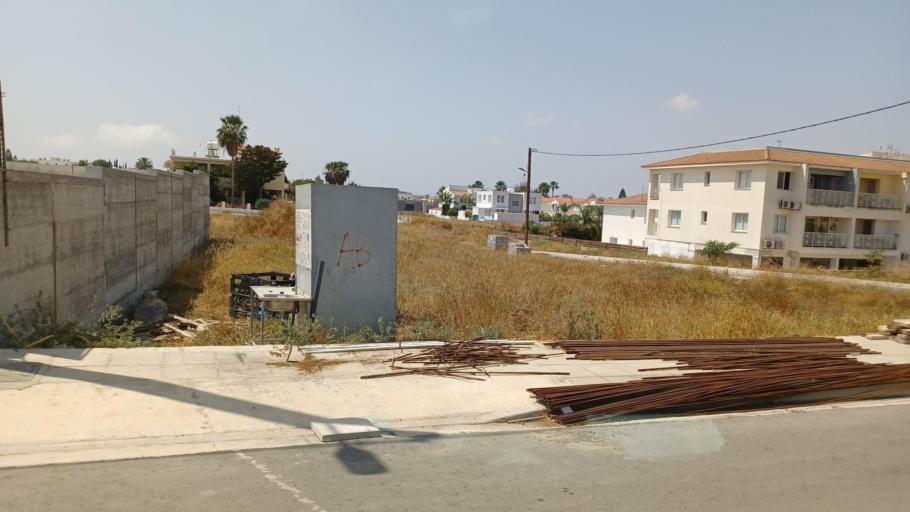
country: CY
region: Ammochostos
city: Paralimni
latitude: 35.0503
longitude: 33.9797
